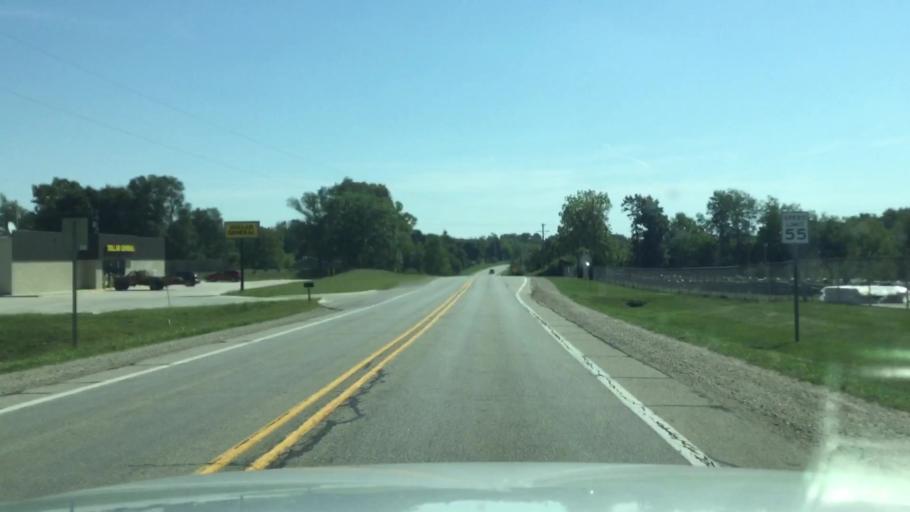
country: US
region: Michigan
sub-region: Lenawee County
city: Manitou Beach-Devils Lake
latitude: 42.0033
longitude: -84.2778
